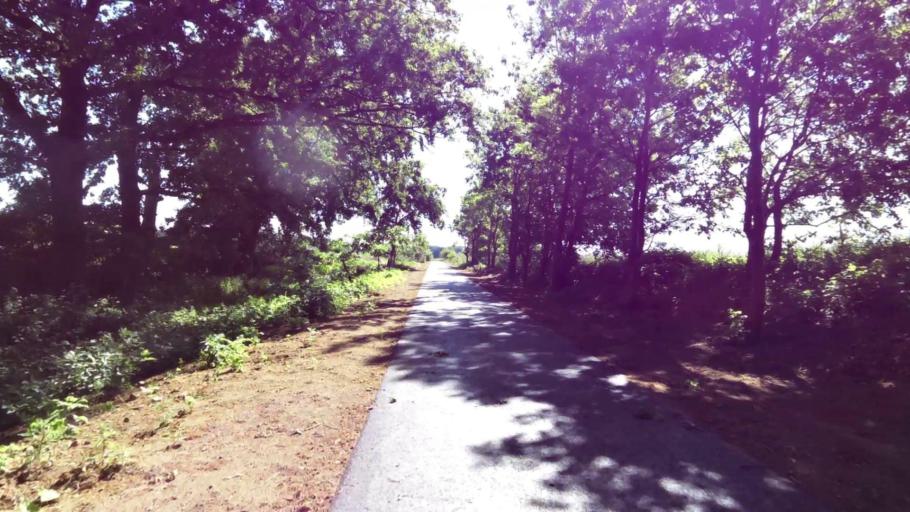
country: PL
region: West Pomeranian Voivodeship
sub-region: Powiat gryfinski
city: Gryfino
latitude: 53.2222
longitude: 14.5608
